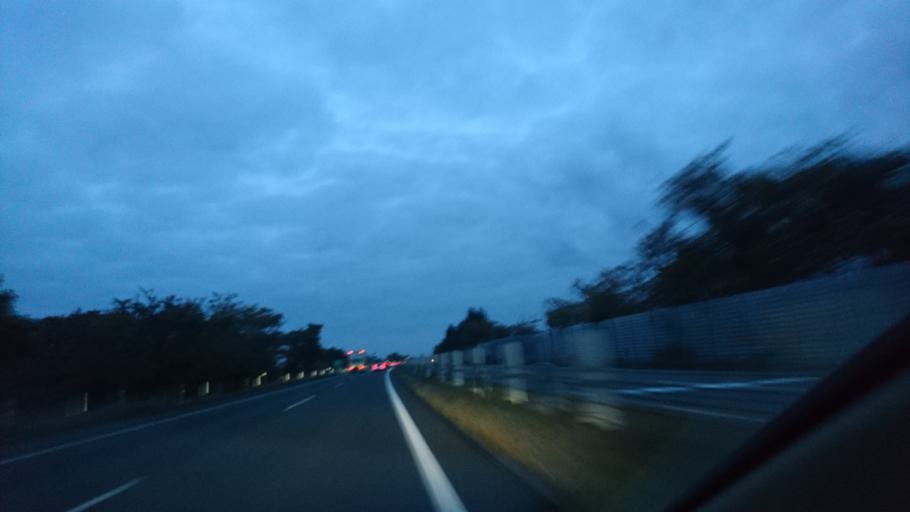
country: JP
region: Iwate
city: Hanamaki
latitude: 39.4869
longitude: 141.1104
